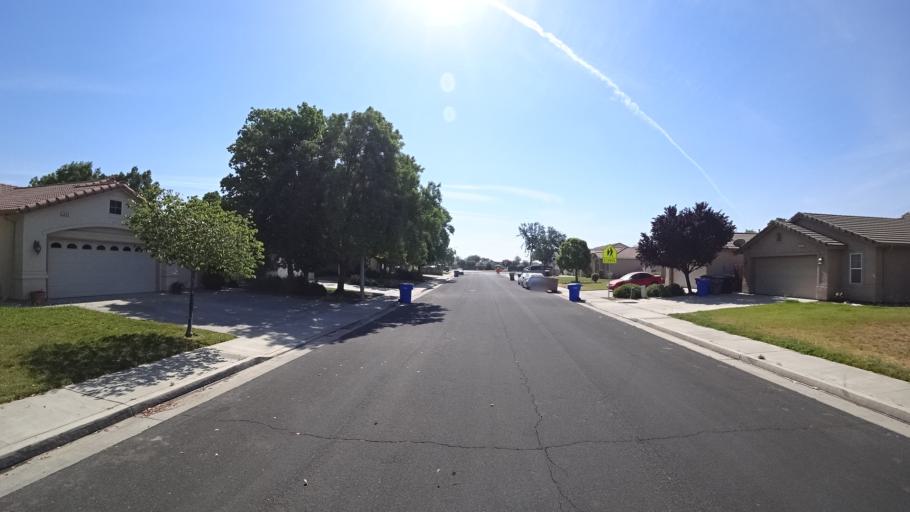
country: US
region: California
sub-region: Kings County
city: Hanford
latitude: 36.3455
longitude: -119.6697
